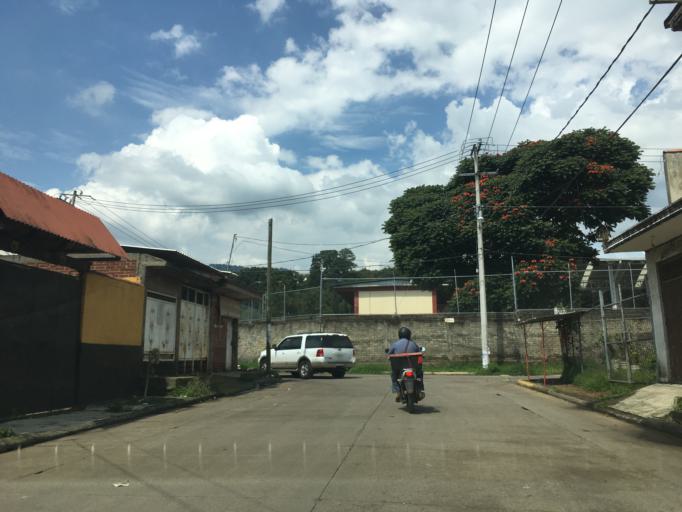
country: MX
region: Michoacan
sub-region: Uruapan
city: Toreo Bajo (El Toreo Bajo)
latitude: 19.4442
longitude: -102.0055
